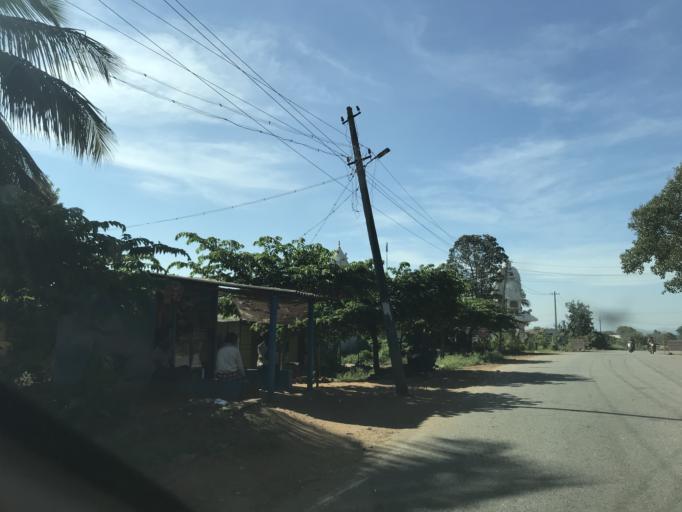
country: IN
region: Karnataka
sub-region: Mysore
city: Sargur
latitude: 12.1333
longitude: 76.5072
